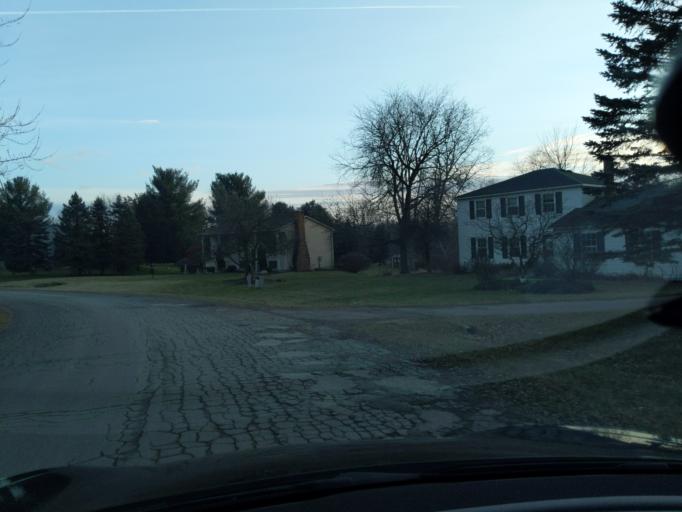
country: US
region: Michigan
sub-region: Livingston County
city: Brighton
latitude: 42.6455
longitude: -83.7236
